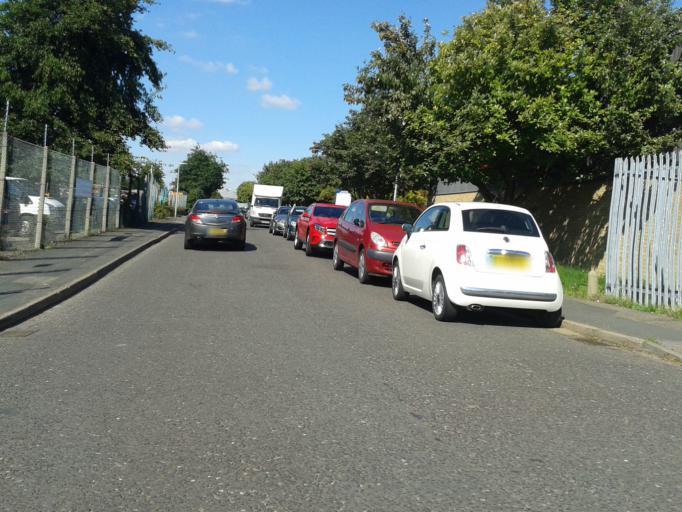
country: GB
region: England
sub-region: Cambridgeshire
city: Cambridge
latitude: 52.2273
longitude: 0.1521
